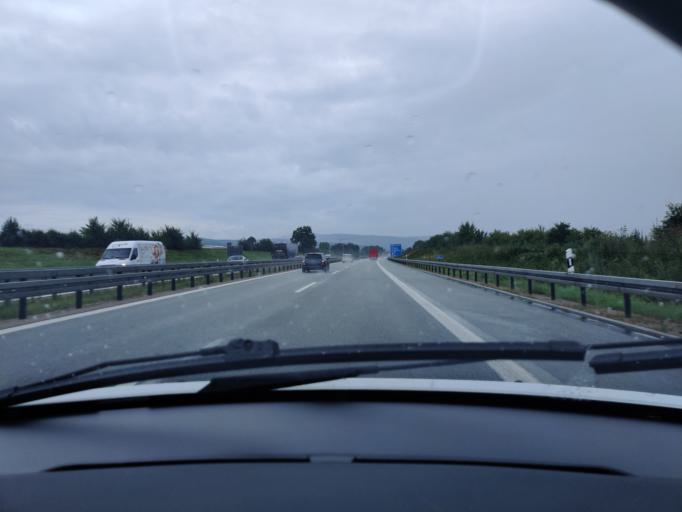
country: DE
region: Bavaria
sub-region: Upper Palatinate
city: Nabburg
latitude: 49.4628
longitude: 12.1949
